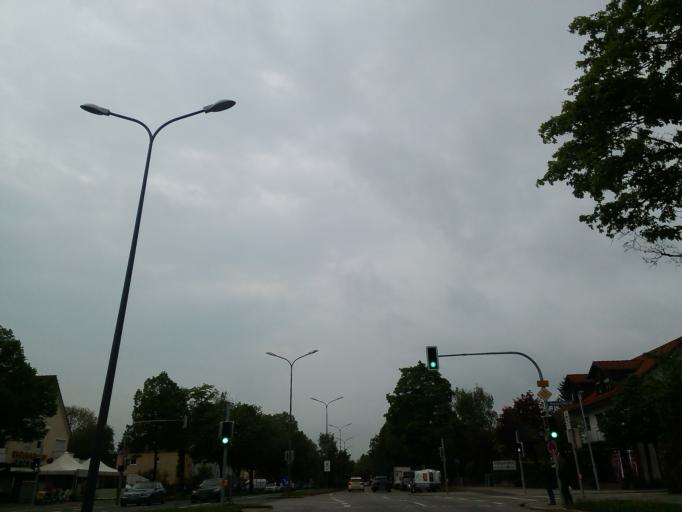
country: DE
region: Bavaria
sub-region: Upper Bavaria
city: Neubiberg
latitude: 48.1236
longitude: 11.6584
